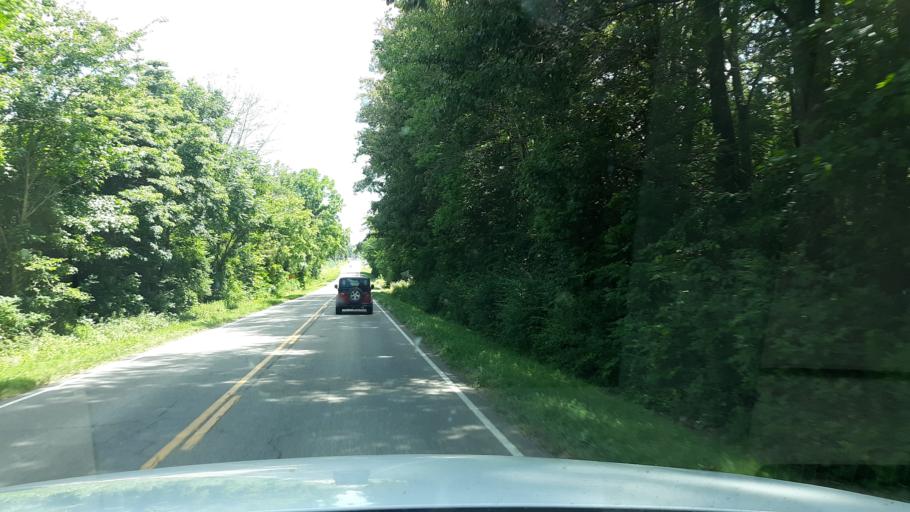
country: US
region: Illinois
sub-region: Saline County
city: Harrisburg
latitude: 37.8496
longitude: -88.6055
